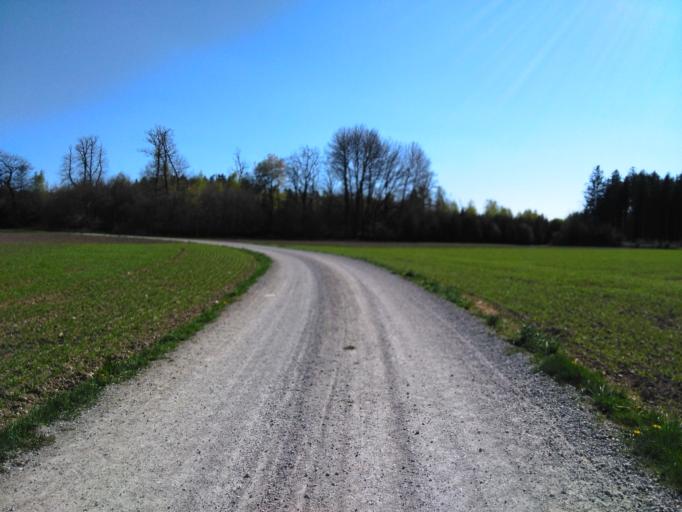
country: DE
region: Bavaria
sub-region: Upper Bavaria
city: Landsberied
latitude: 48.2024
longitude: 11.2038
